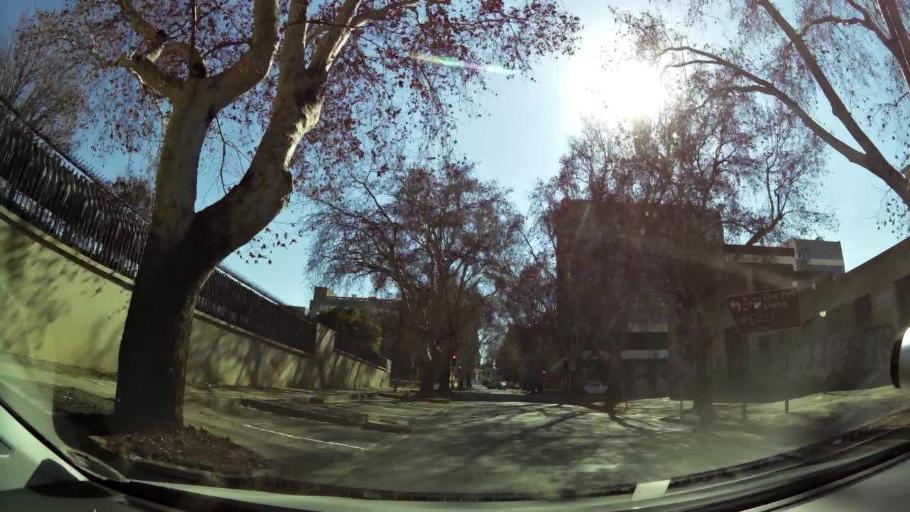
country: ZA
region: Gauteng
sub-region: City of Johannesburg Metropolitan Municipality
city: Johannesburg
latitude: -26.1946
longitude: 28.0301
